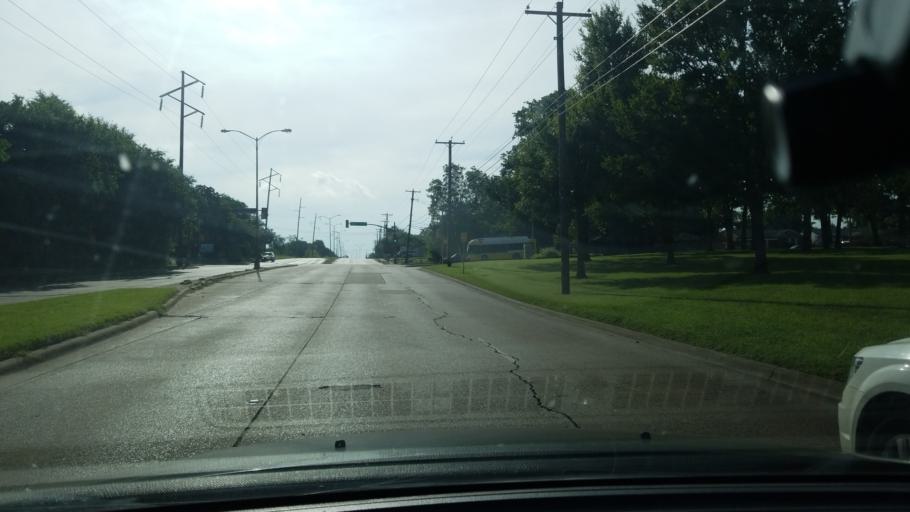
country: US
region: Texas
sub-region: Dallas County
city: Balch Springs
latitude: 32.7195
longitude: -96.6666
